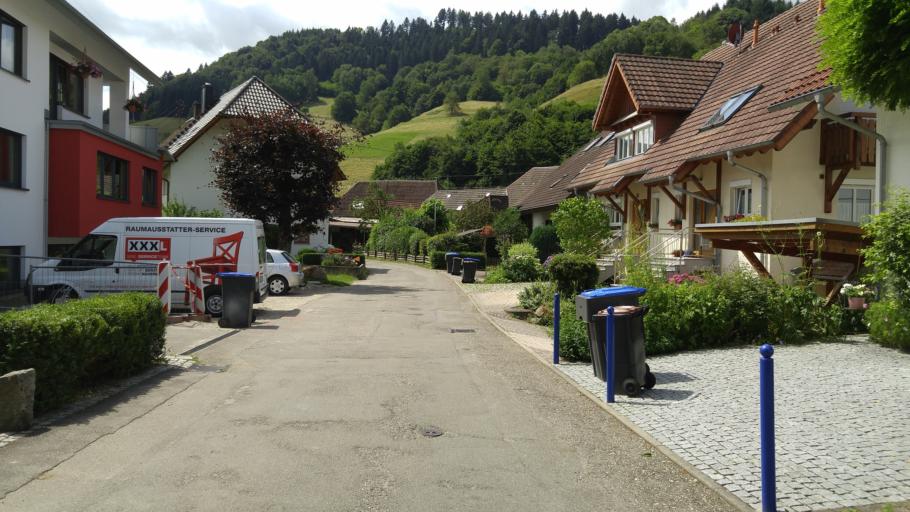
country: DE
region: Baden-Wuerttemberg
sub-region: Freiburg Region
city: Muenstertal/Schwarzwald
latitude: 47.8515
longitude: 7.7888
